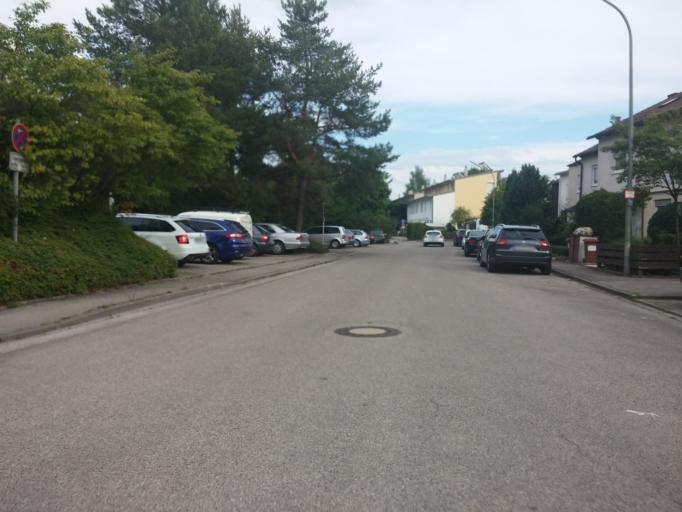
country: DE
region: Bavaria
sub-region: Upper Bavaria
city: Haar
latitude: 48.1137
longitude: 11.7120
